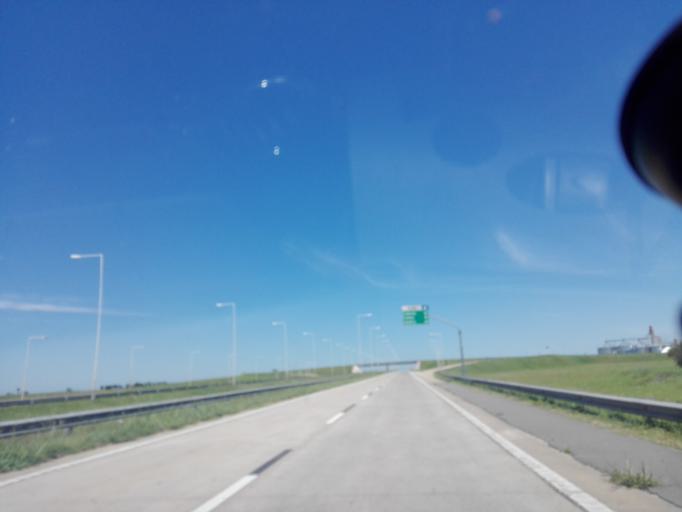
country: AR
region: Santa Fe
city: Carcarana
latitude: -32.8676
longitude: -61.2472
